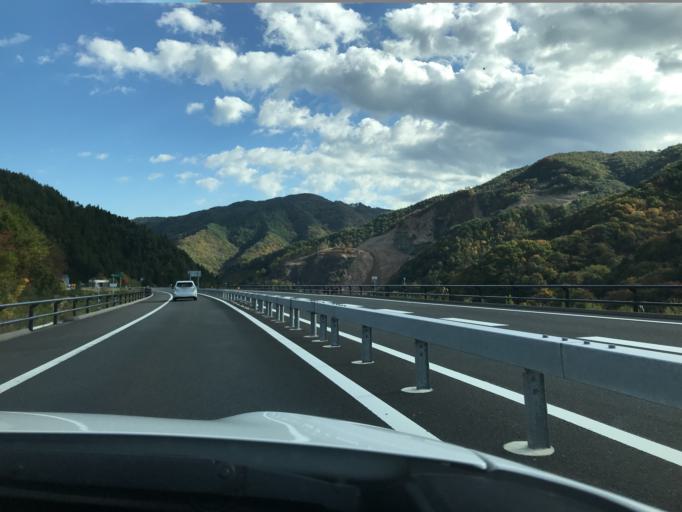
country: JP
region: Miyagi
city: Marumori
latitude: 37.7865
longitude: 140.7916
